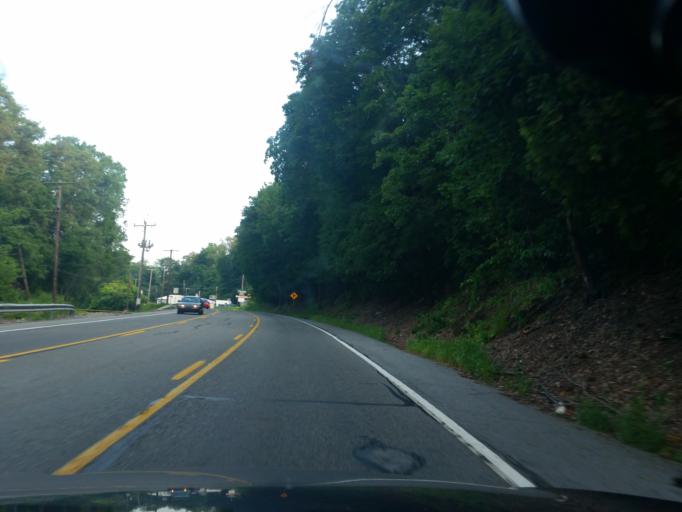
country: US
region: Pennsylvania
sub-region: Cumberland County
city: Enola
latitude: 40.2838
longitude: -76.9291
